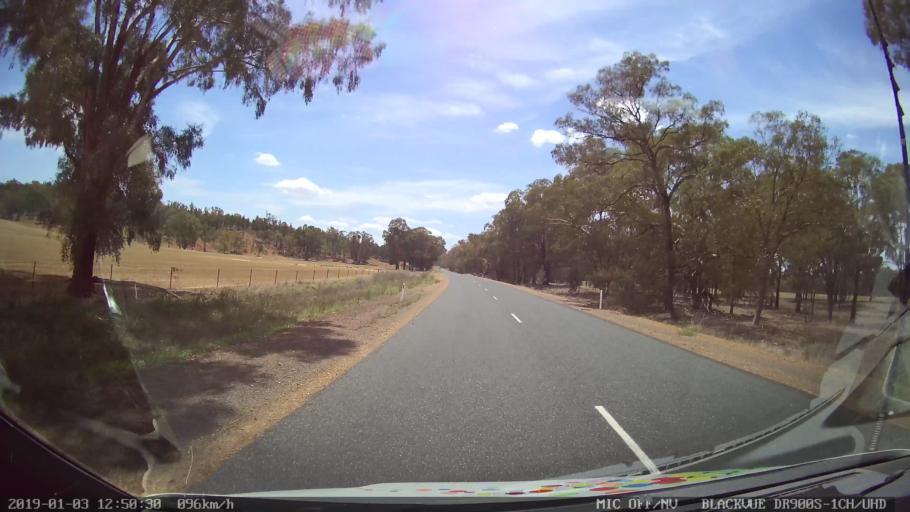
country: AU
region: New South Wales
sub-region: Weddin
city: Grenfell
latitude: -33.6909
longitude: 148.2712
